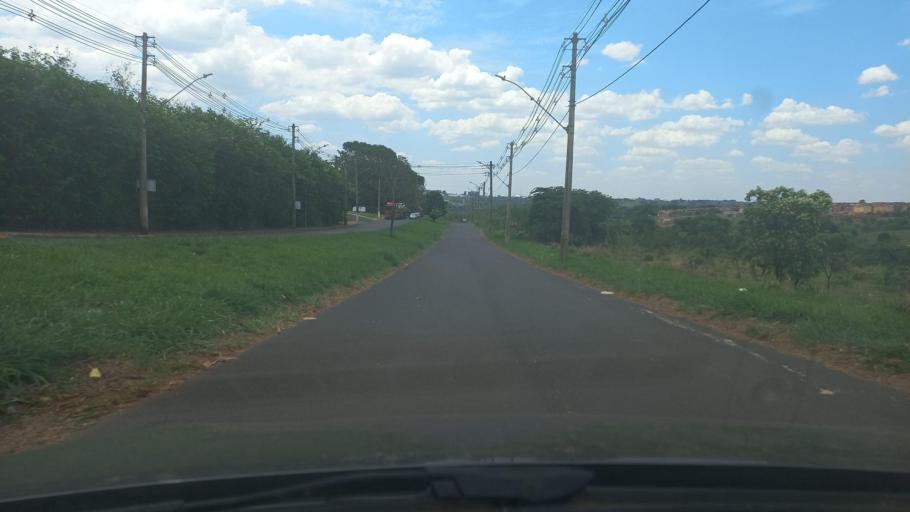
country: BR
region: Minas Gerais
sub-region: Uberaba
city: Uberaba
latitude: -19.7412
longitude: -47.9740
